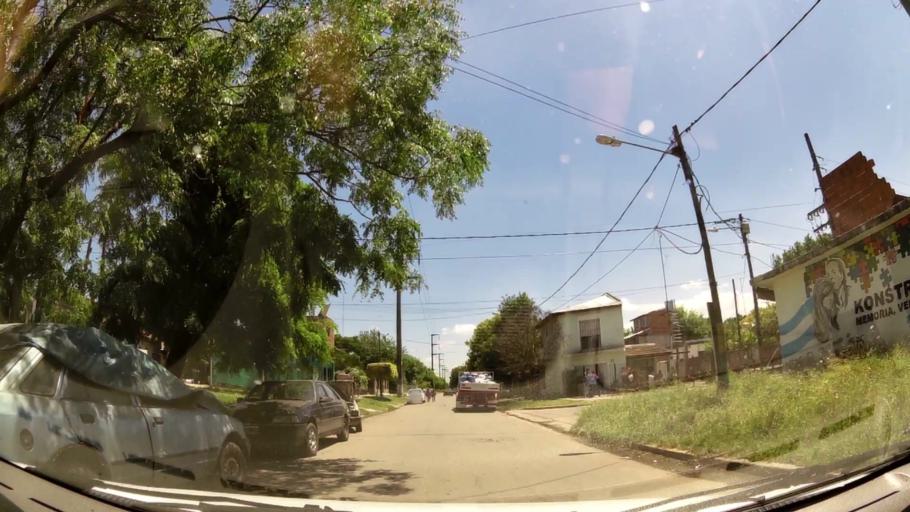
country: AR
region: Buenos Aires
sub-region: Partido de Merlo
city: Merlo
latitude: -34.6481
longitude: -58.7044
